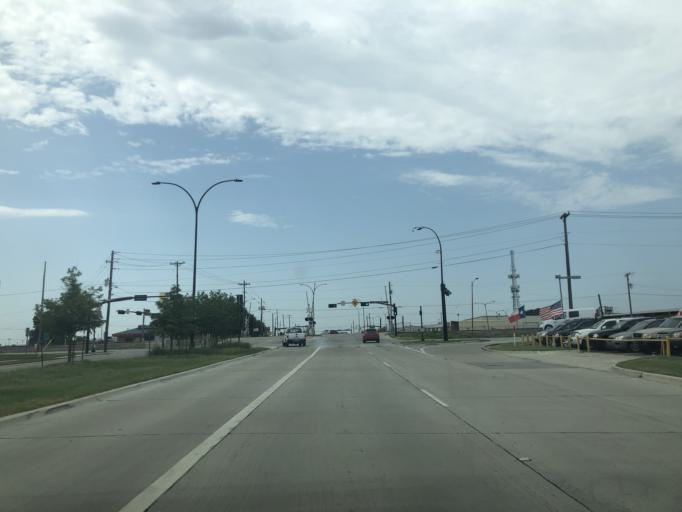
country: US
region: Texas
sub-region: Dallas County
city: Grand Prairie
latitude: 32.7402
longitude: -97.0460
